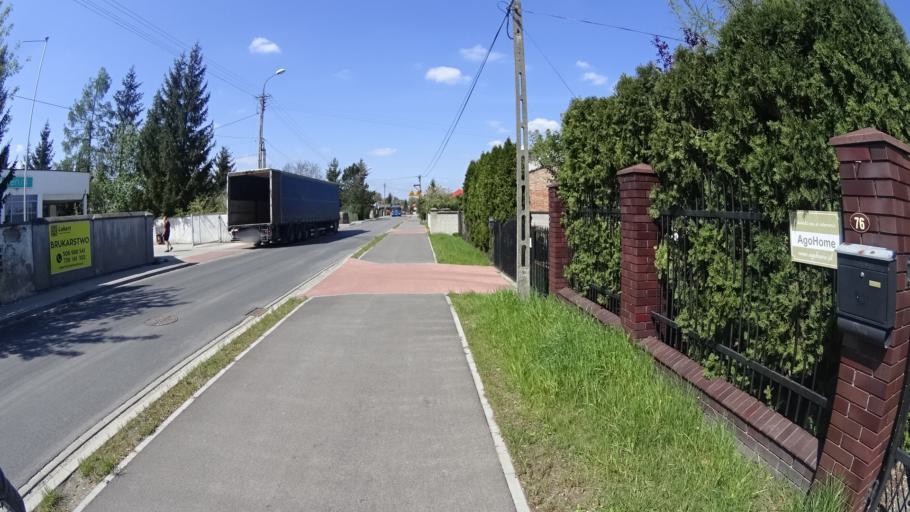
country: PL
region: Masovian Voivodeship
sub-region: Powiat warszawski zachodni
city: Hornowek
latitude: 52.2723
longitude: 20.8071
